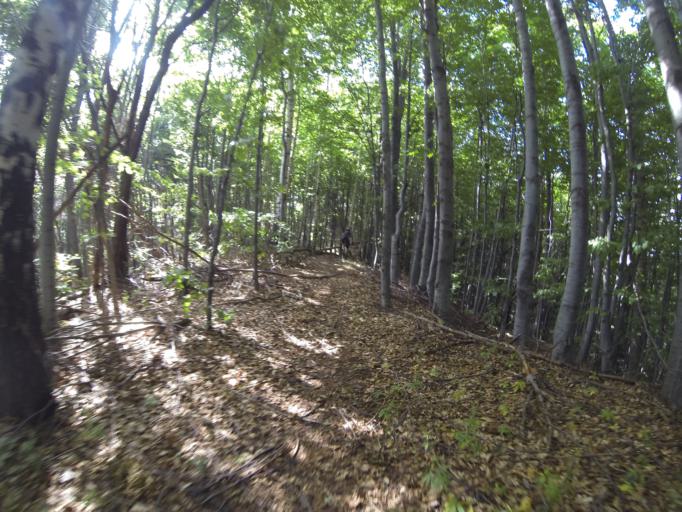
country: RO
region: Valcea
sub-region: Oras Baile Olanesti
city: Cheia
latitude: 45.2423
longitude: 24.1683
